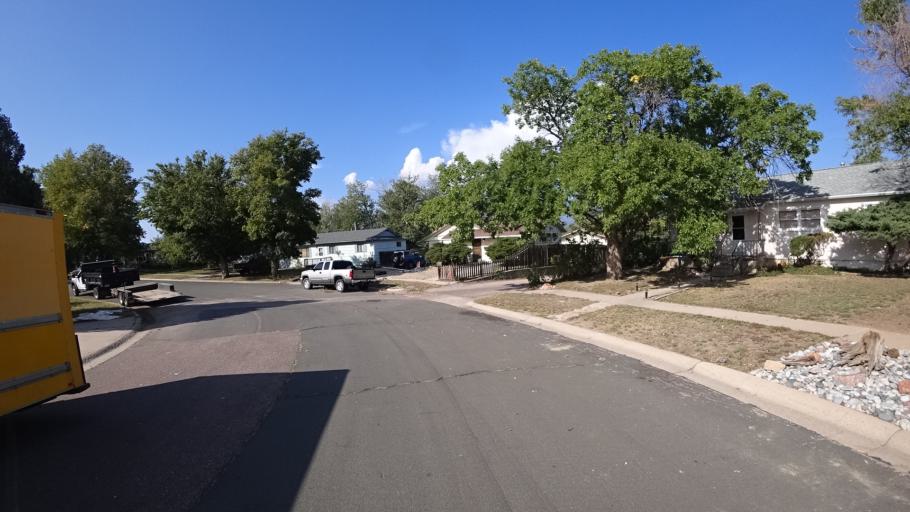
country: US
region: Colorado
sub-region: El Paso County
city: Colorado Springs
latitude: 38.8536
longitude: -104.7745
